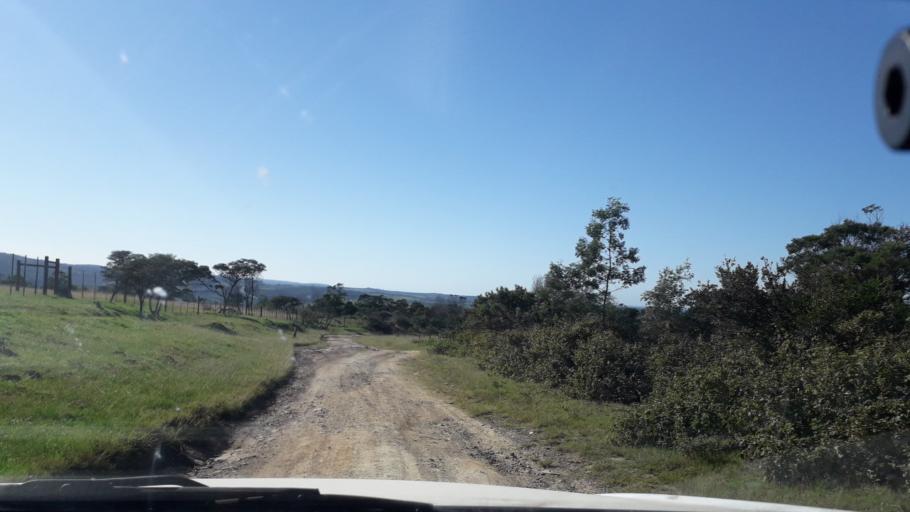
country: ZA
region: Eastern Cape
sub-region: Buffalo City Metropolitan Municipality
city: East London
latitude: -32.8412
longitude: 27.9769
